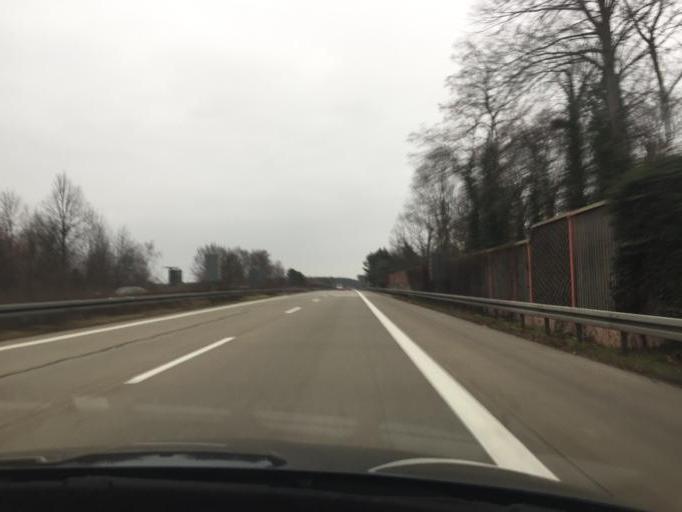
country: DE
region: Brandenburg
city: Lubbenau
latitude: 51.8303
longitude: 13.9872
